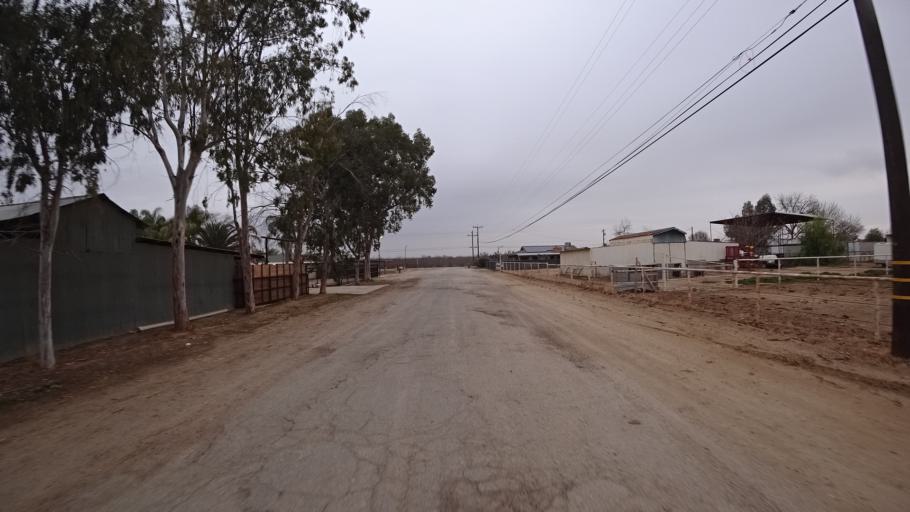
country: US
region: California
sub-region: Kern County
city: Lamont
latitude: 35.3197
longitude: -118.9334
